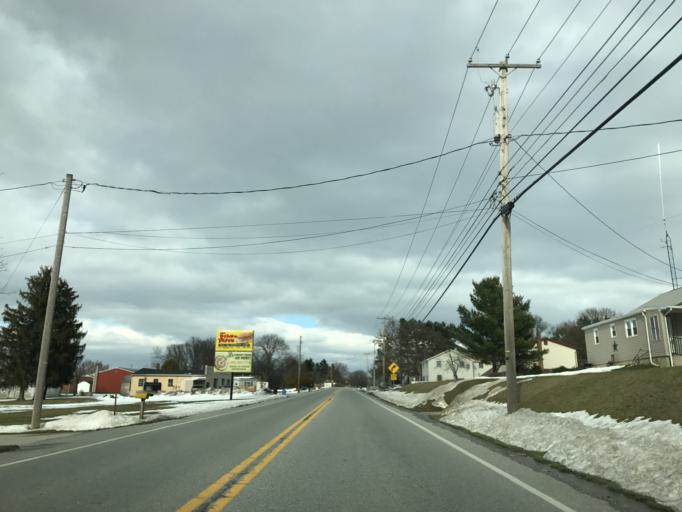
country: US
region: Pennsylvania
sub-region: York County
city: Spring Grove
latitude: 39.8521
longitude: -76.8920
